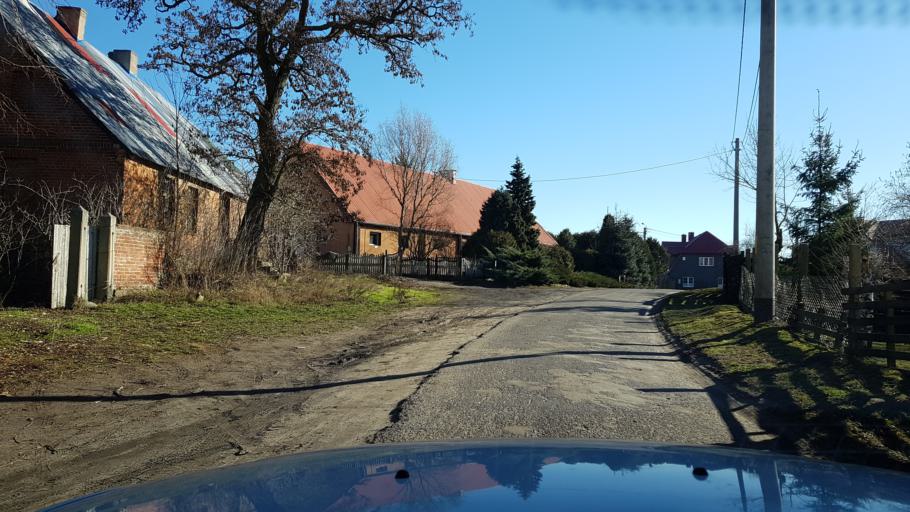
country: PL
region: West Pomeranian Voivodeship
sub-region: Powiat pyrzycki
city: Przelewice
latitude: 53.0244
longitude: 15.0777
